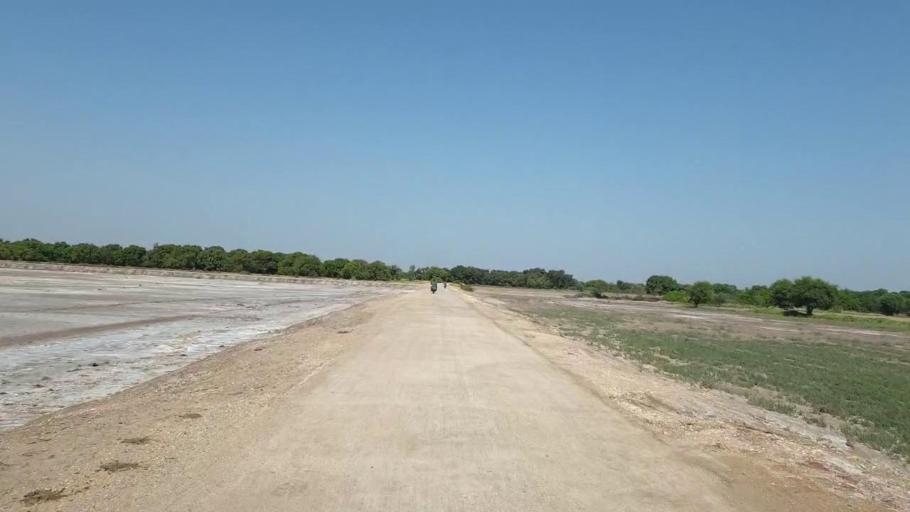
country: PK
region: Sindh
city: Tando Jam
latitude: 25.4197
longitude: 68.4577
